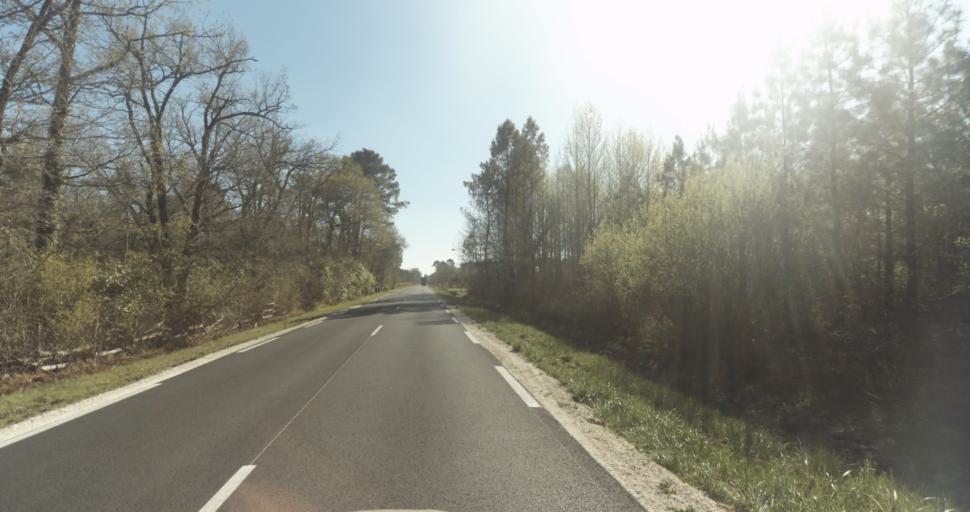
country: FR
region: Aquitaine
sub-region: Departement de la Gironde
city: Martignas-sur-Jalle
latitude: 44.7948
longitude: -0.8577
